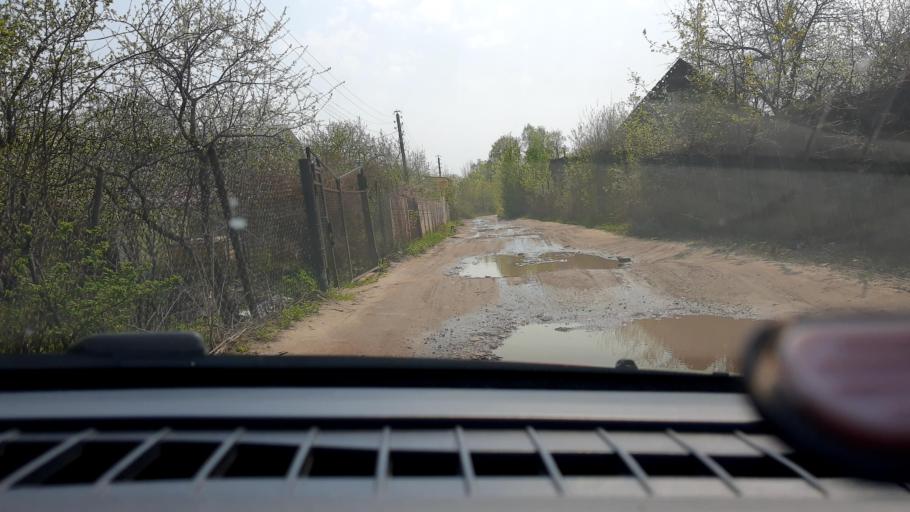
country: RU
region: Nizjnij Novgorod
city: Gorbatovka
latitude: 56.2683
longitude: 43.7842
